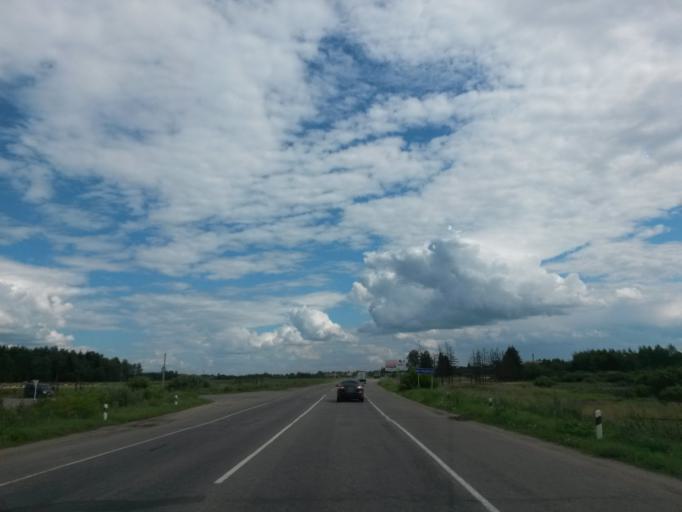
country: RU
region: Ivanovo
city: Novo-Talitsy
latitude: 57.0129
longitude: 40.8231
